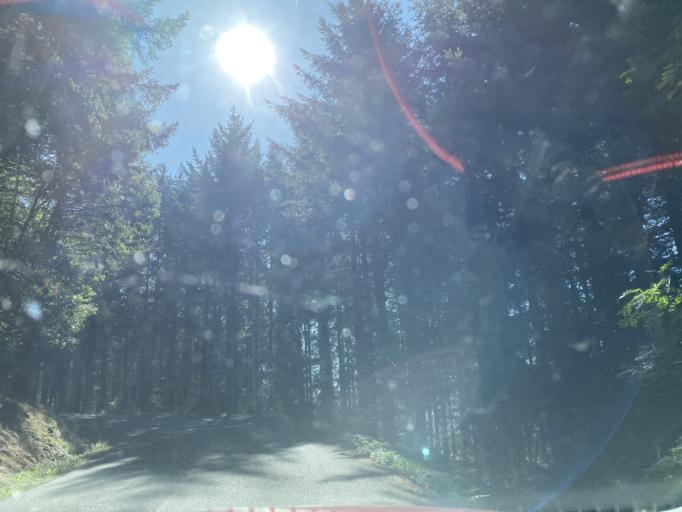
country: FR
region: Rhone-Alpes
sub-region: Departement de la Loire
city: Noiretable
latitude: 45.8238
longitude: 3.7729
